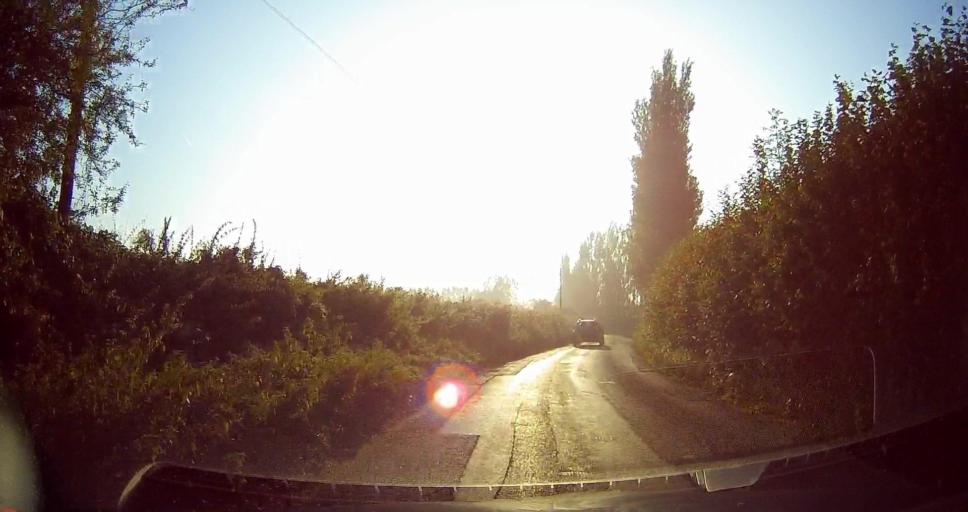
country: GB
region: England
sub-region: Kent
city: Kennington
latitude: 51.1873
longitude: 0.8987
